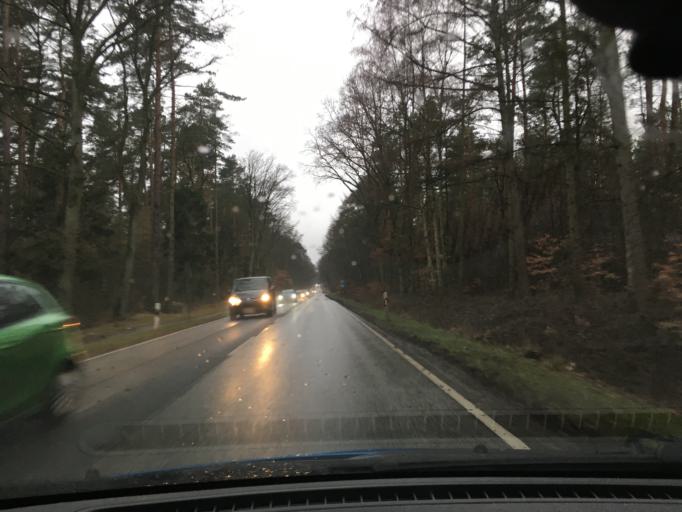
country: DE
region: Schleswig-Holstein
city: Schnakenbek
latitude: 53.3884
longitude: 10.4922
